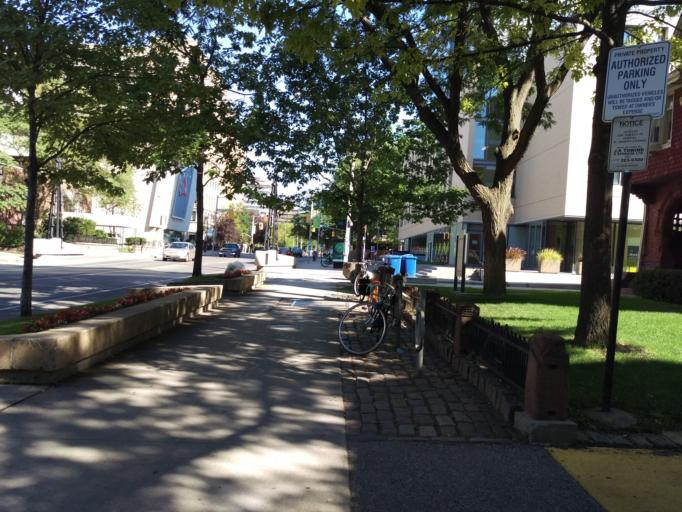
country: CA
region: Ontario
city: Toronto
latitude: 43.6668
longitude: -79.3994
